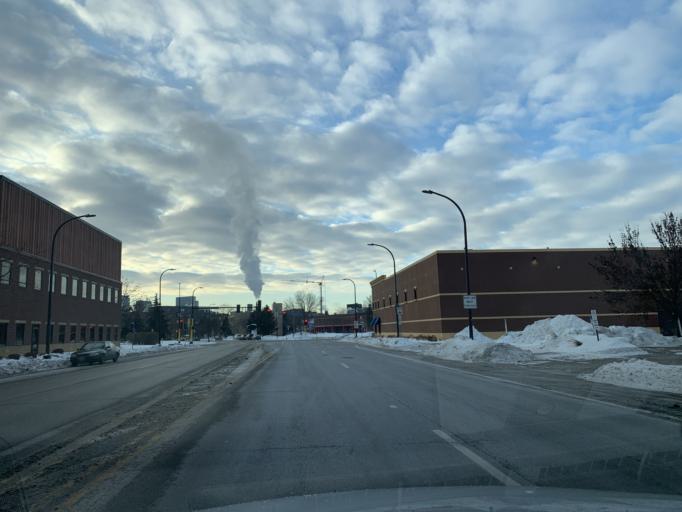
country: US
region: Minnesota
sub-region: Hennepin County
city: Minneapolis
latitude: 44.9930
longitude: -93.2815
